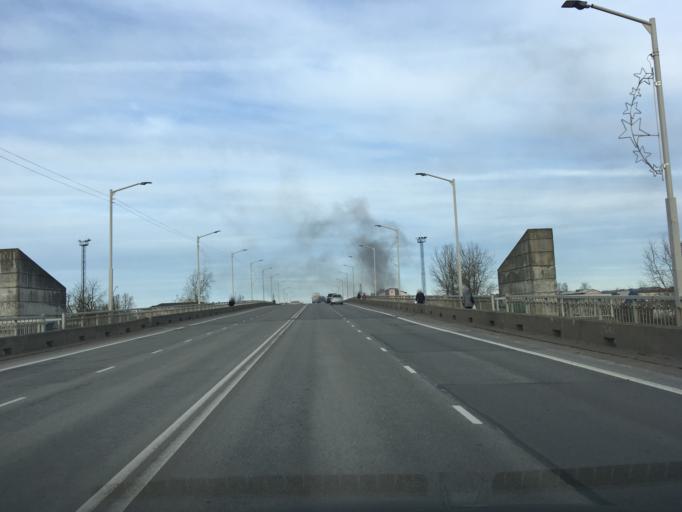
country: EE
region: Ida-Virumaa
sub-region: Narva linn
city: Narva
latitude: 59.3705
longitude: 28.1847
